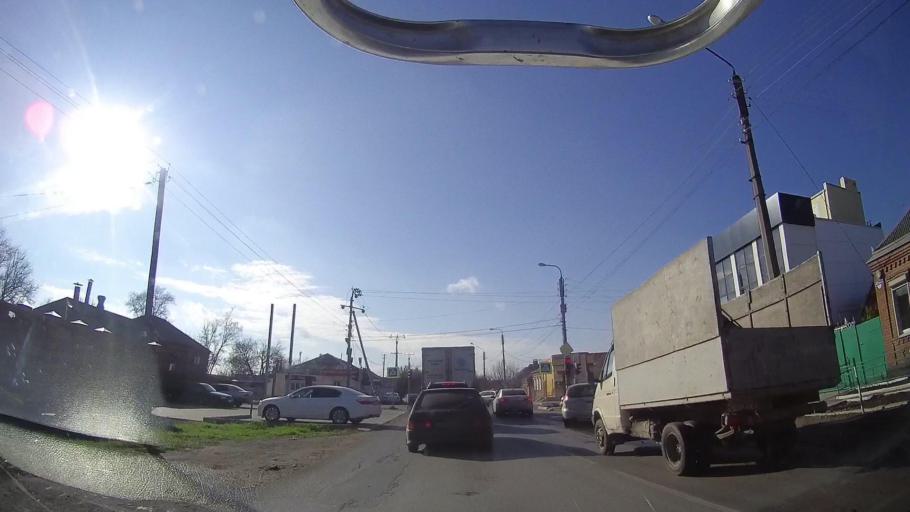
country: RU
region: Rostov
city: Bataysk
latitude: 47.1302
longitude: 39.6970
